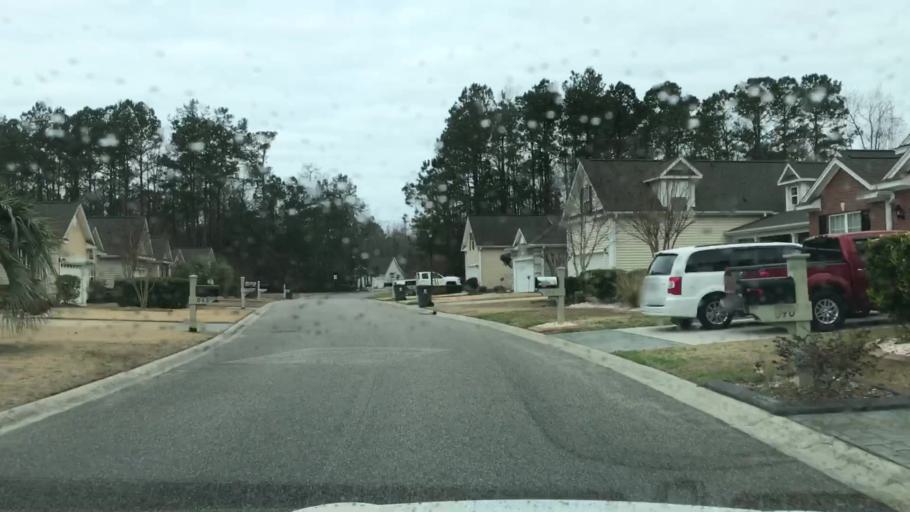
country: US
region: South Carolina
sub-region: Horry County
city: Red Hill
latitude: 33.7769
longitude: -79.0080
